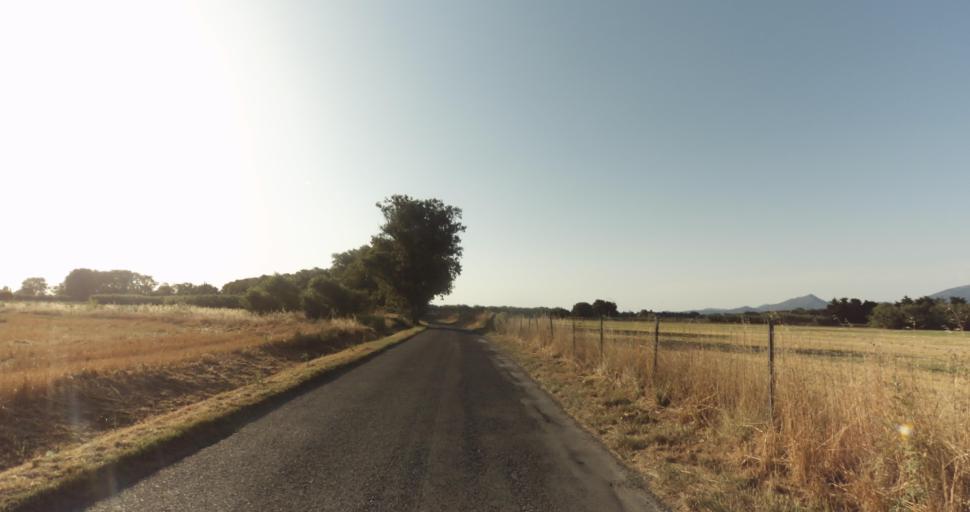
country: FR
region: Languedoc-Roussillon
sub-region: Departement des Pyrenees-Orientales
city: Latour-Bas-Elne
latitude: 42.5965
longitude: 3.0172
